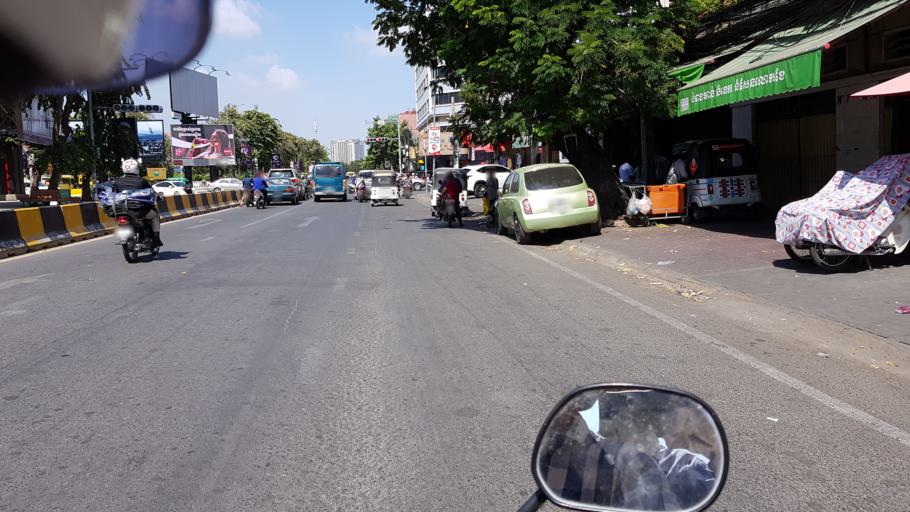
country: KH
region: Phnom Penh
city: Phnom Penh
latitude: 11.5675
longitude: 104.9115
